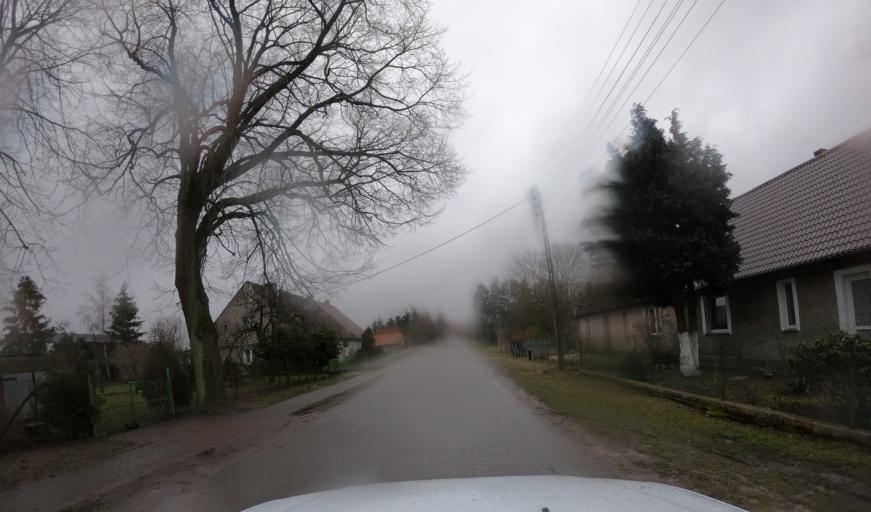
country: PL
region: West Pomeranian Voivodeship
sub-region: Powiat kamienski
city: Kamien Pomorski
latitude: 53.9007
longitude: 14.8265
